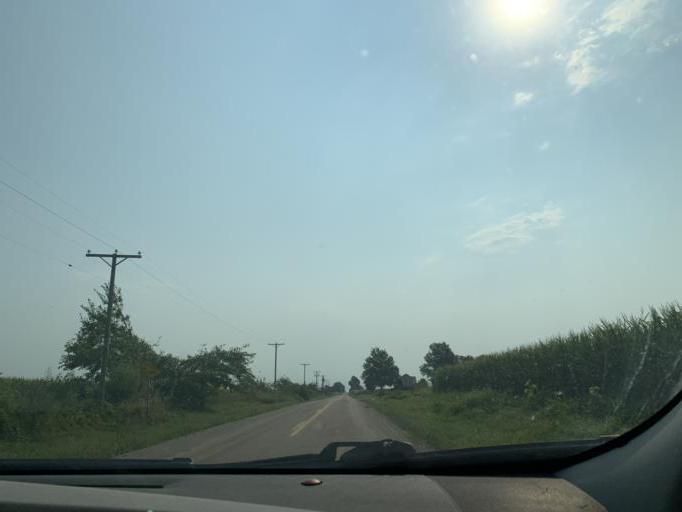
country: US
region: Illinois
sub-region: Carroll County
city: Milledgeville
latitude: 41.8480
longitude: -89.8379
